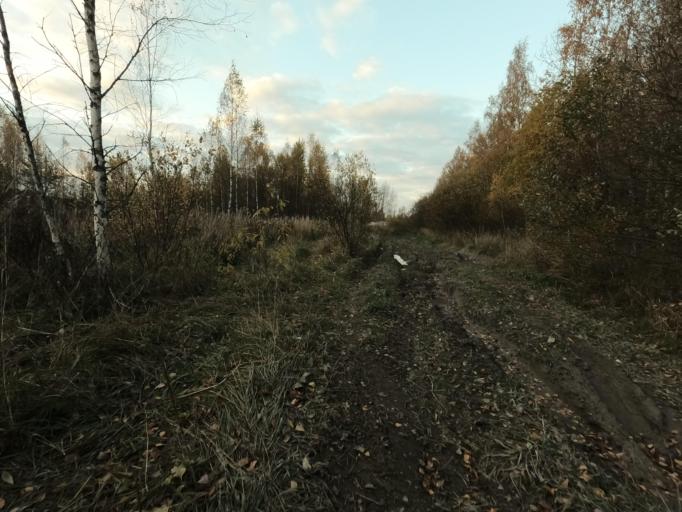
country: RU
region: Leningrad
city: Mga
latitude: 59.8156
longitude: 31.1780
